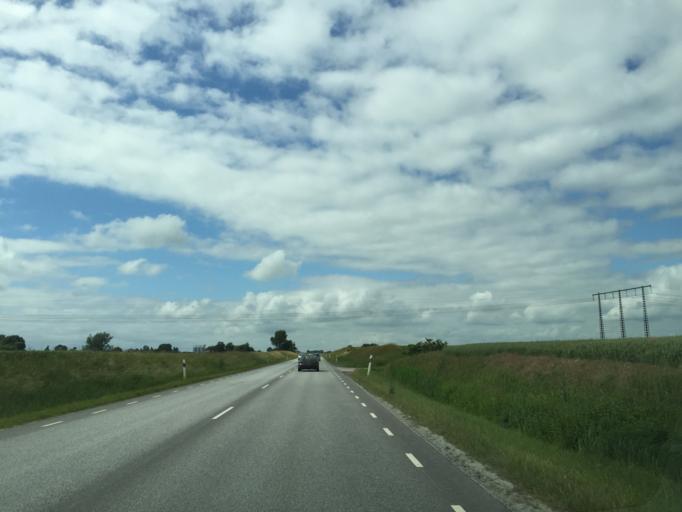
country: SE
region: Skane
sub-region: Staffanstorps Kommun
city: Staffanstorp
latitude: 55.6597
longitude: 13.2141
